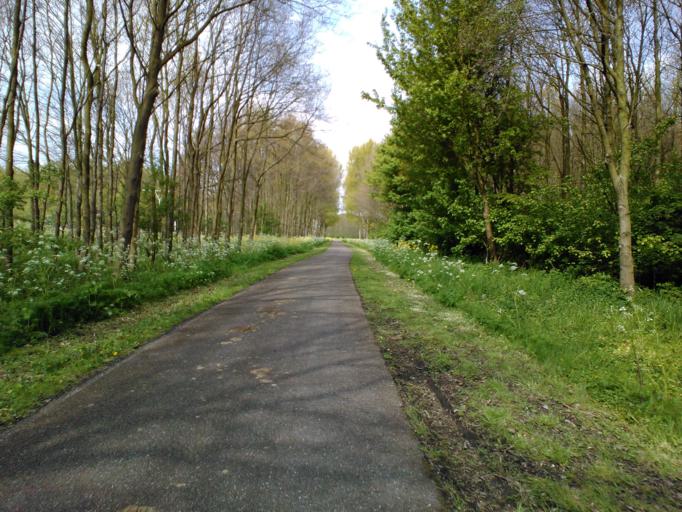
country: NL
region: South Holland
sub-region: Gemeente Maassluis
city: Maassluis
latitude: 51.9097
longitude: 4.2871
